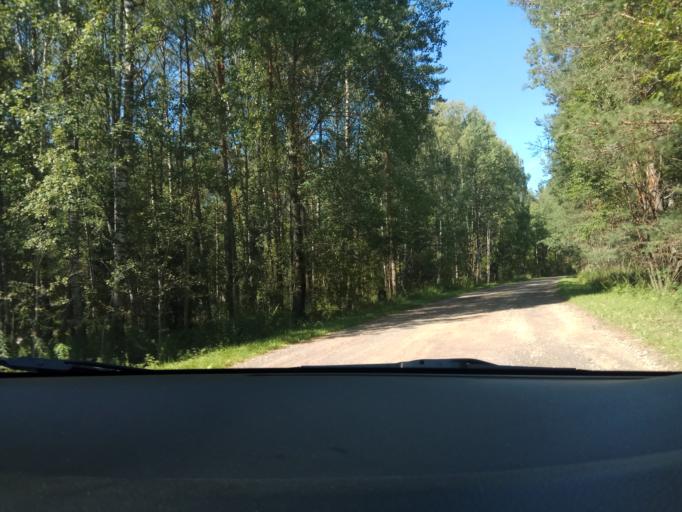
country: RU
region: Vladimir
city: Dobryatino
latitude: 55.7385
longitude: 41.4306
